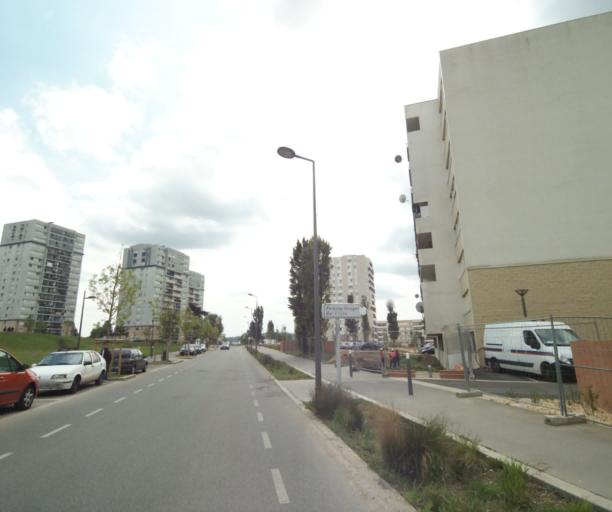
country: FR
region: Ile-de-France
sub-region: Departement des Yvelines
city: Les Mureaux
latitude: 48.9780
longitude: 1.9198
